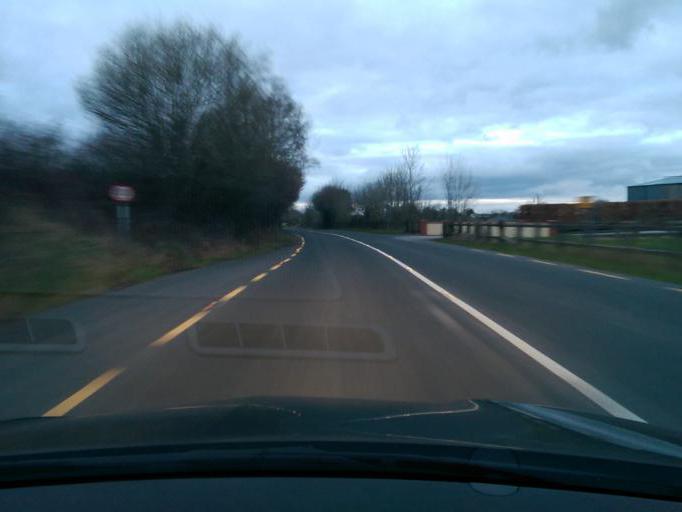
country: IE
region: Connaught
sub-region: County Galway
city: Portumna
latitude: 53.1264
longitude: -8.2443
